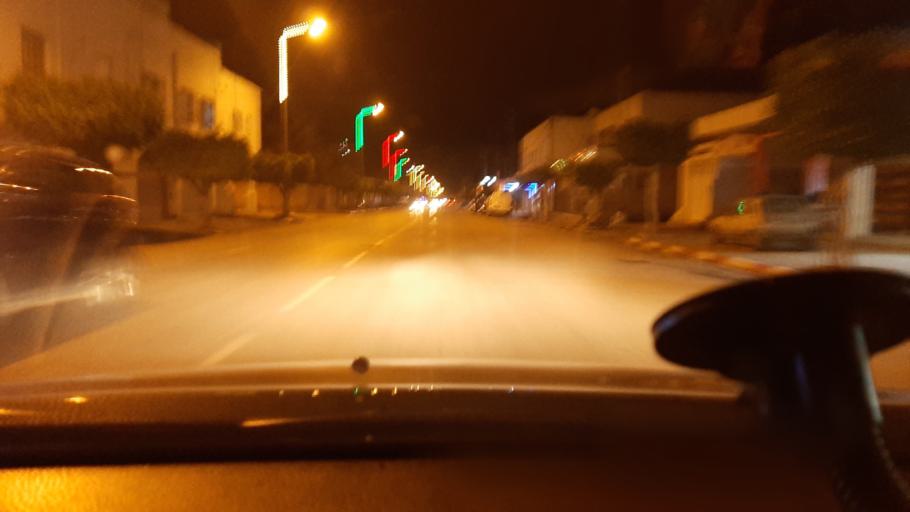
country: TN
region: Safaqis
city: Sfax
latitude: 34.7804
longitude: 10.7242
